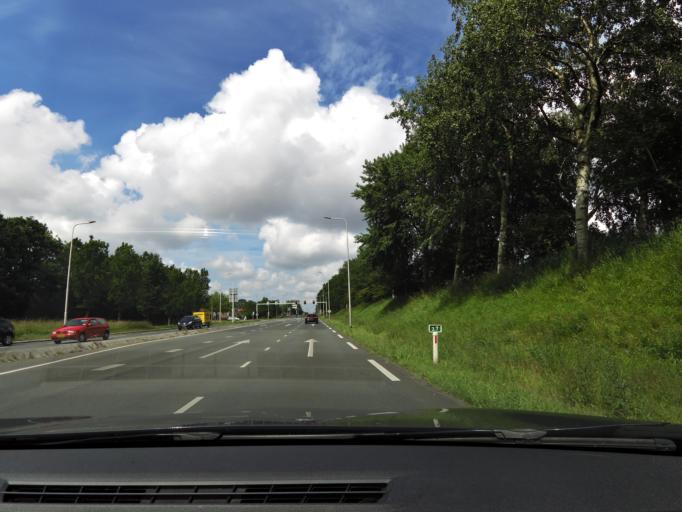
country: NL
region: Zeeland
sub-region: Gemeente Vlissingen
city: Vlissingen
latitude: 51.4618
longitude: 3.5917
